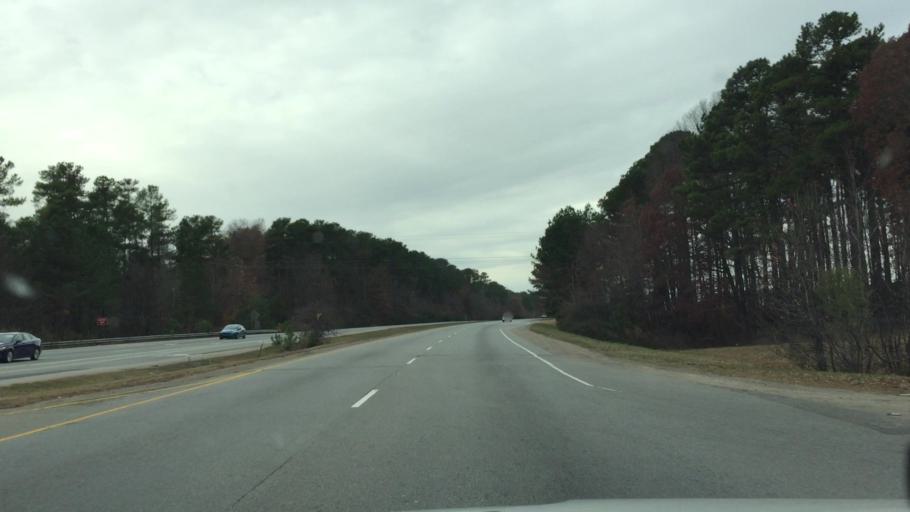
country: US
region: North Carolina
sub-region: Wake County
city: Apex
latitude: 35.7443
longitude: -78.8241
